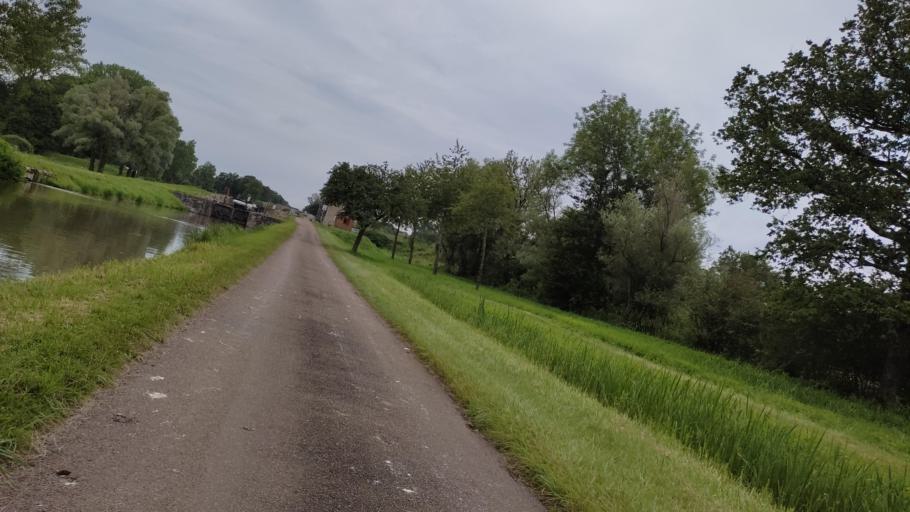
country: FR
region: Bourgogne
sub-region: Departement de la Nievre
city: Chatillon-en-Bazois
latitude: 47.1067
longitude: 3.6330
